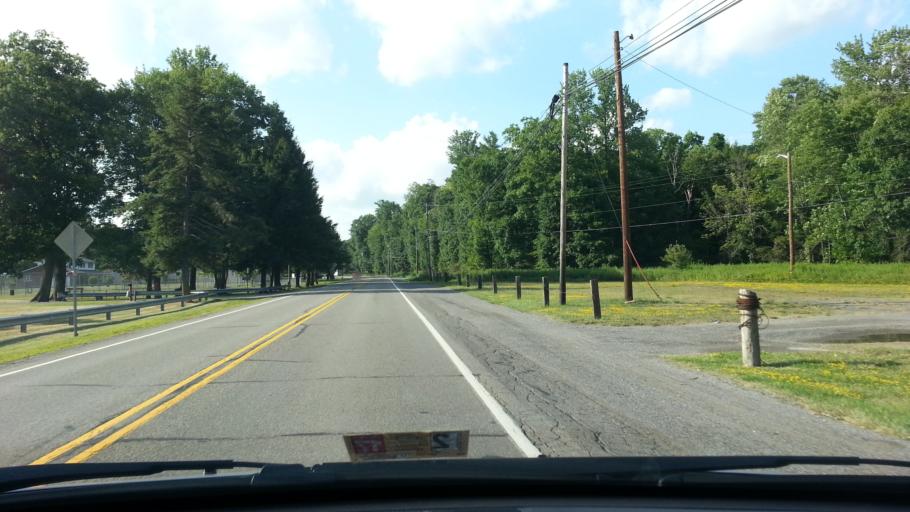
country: US
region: Pennsylvania
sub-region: Elk County
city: Saint Marys
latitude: 41.2769
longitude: -78.4977
